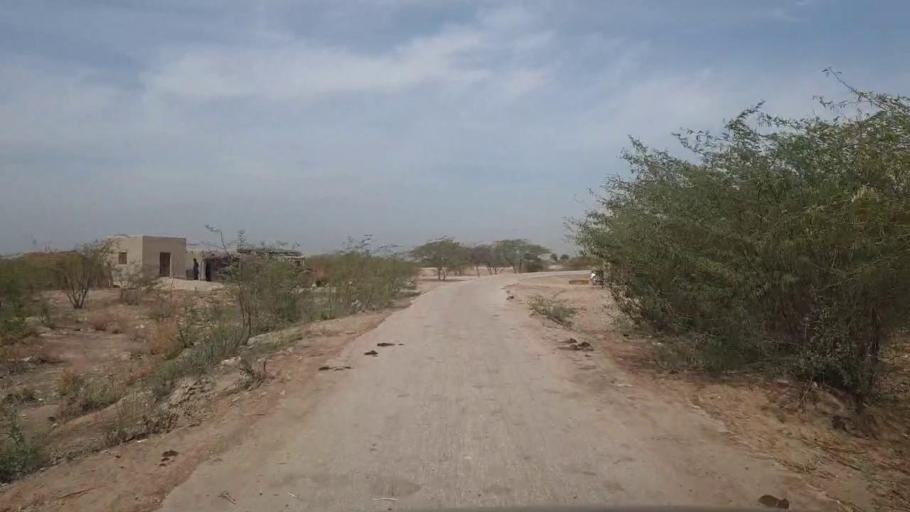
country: PK
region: Sindh
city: Kunri
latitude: 25.2365
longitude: 69.6693
